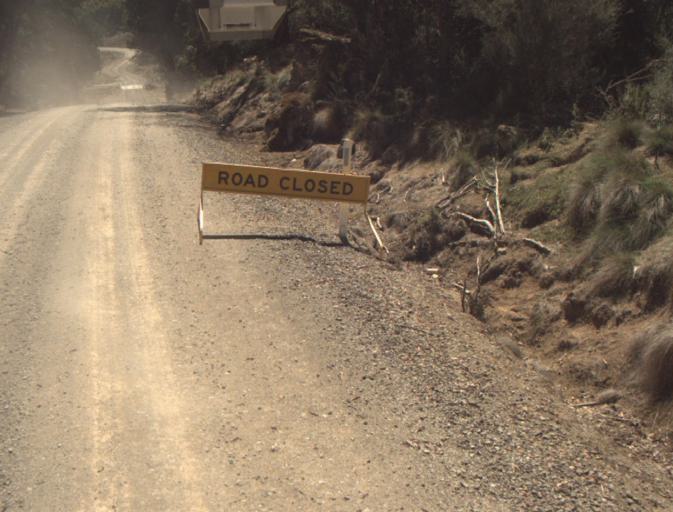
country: AU
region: Tasmania
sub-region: Dorset
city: Scottsdale
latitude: -41.3231
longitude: 147.4652
